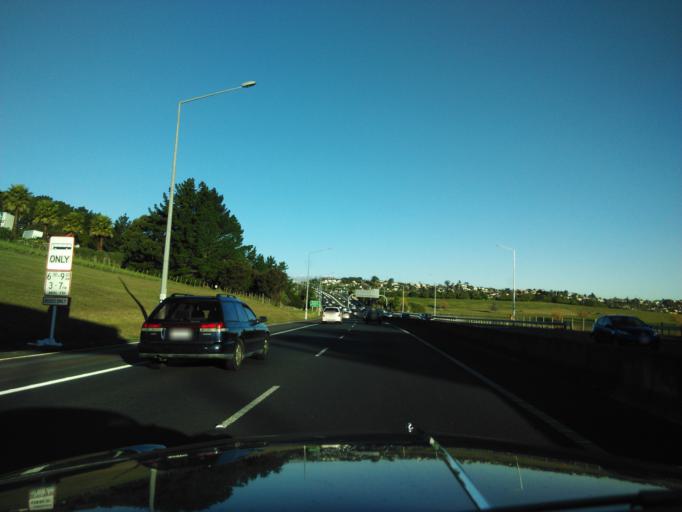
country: NZ
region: Auckland
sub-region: Auckland
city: Rothesay Bay
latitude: -36.7437
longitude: 174.7209
